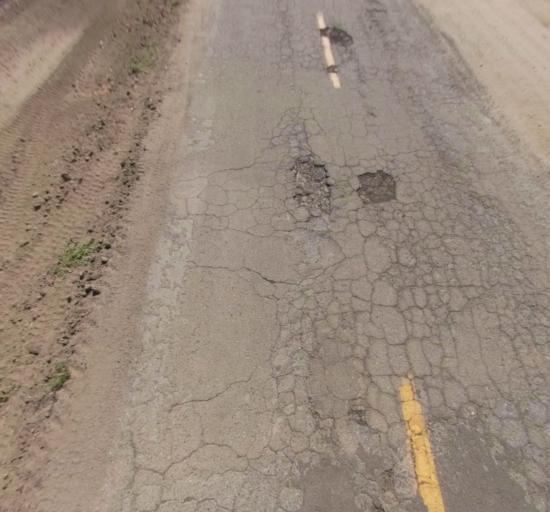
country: US
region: California
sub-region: Madera County
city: Madera
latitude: 36.9456
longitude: -120.1237
